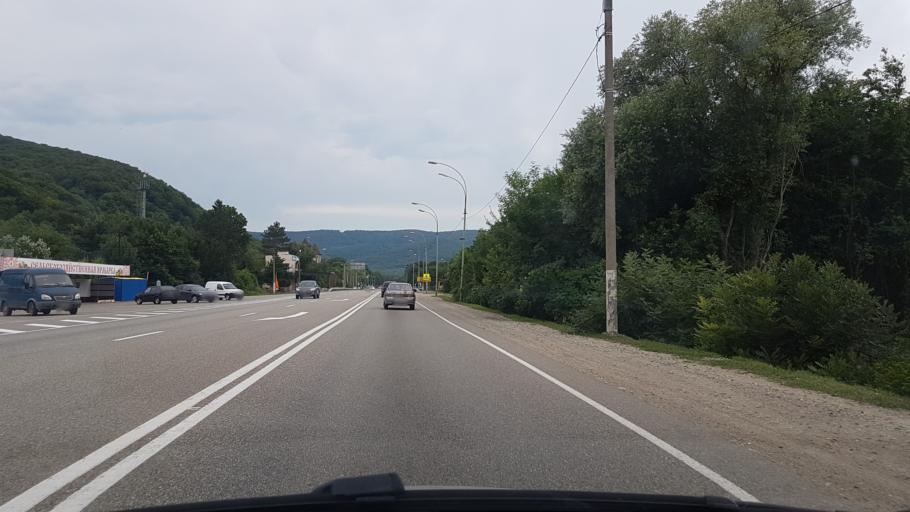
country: RU
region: Krasnodarskiy
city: Goryachiy Klyuch
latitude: 44.6256
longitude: 39.0920
